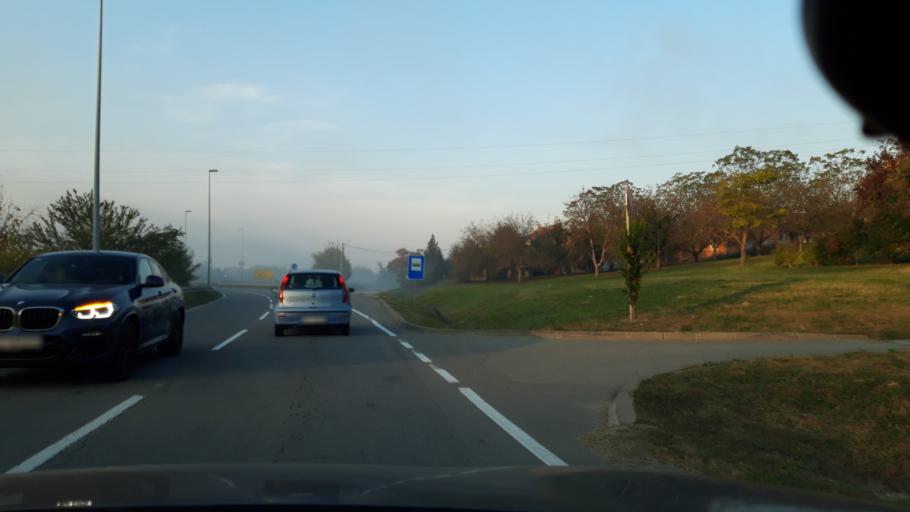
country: RS
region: Autonomna Pokrajina Vojvodina
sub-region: Juznobacki Okrug
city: Novi Sad
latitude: 45.2095
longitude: 19.8410
